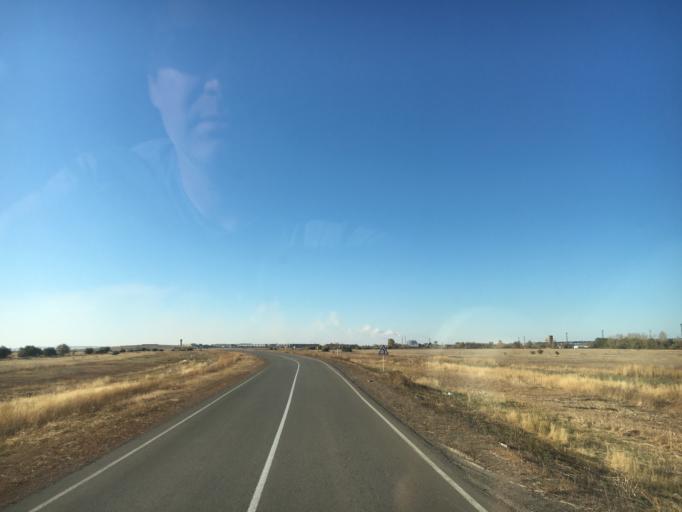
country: KZ
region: Qaraghandy
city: Aqtau
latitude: 50.1953
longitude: 73.0925
